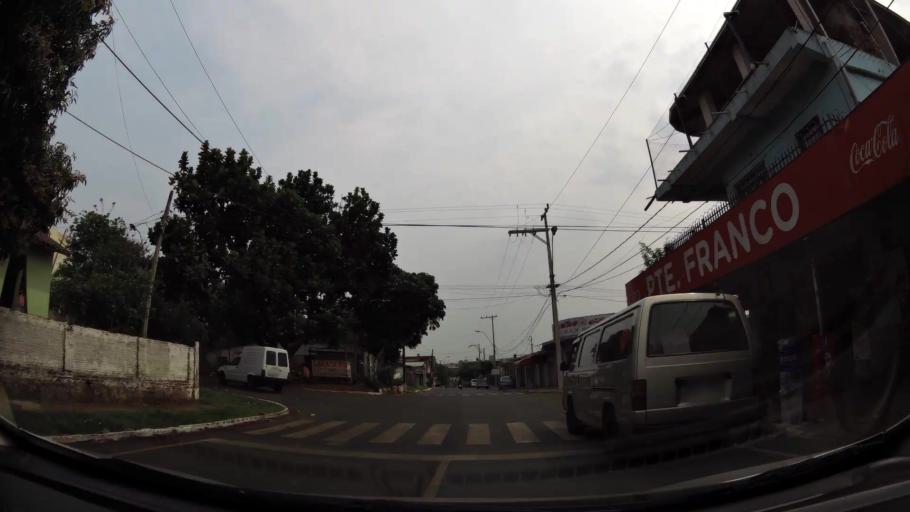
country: BR
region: Parana
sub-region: Foz Do Iguacu
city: Foz do Iguacu
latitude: -25.5520
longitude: -54.6066
